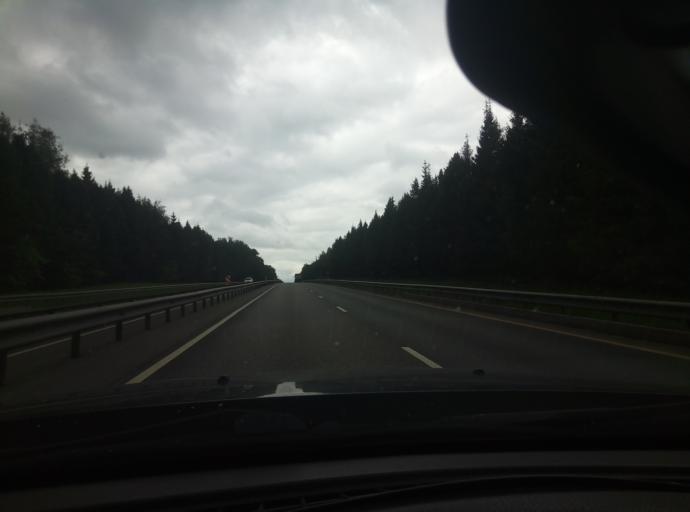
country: RU
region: Kaluga
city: Maloyaroslavets
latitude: 54.9913
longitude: 36.5131
